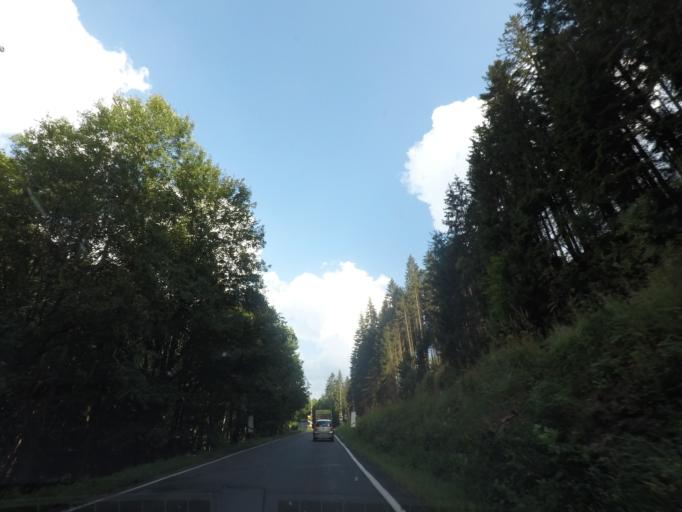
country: CZ
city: Radvanice
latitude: 50.6024
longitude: 16.0101
